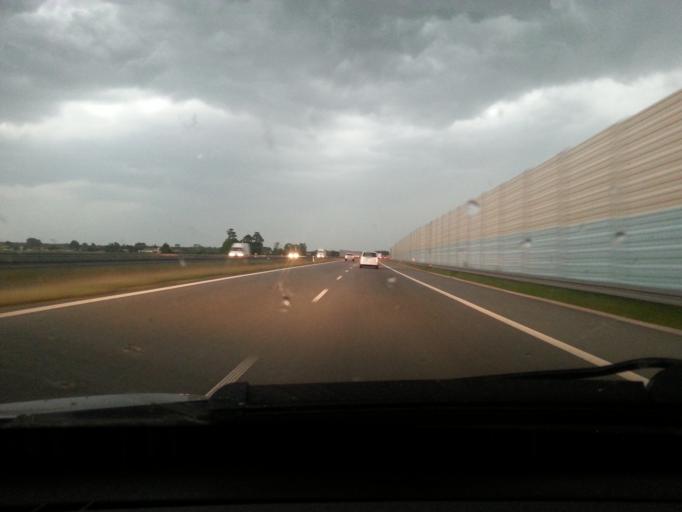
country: PL
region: Lodz Voivodeship
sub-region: powiat Lowicki
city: Lyszkowice
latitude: 51.9725
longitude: 19.8718
